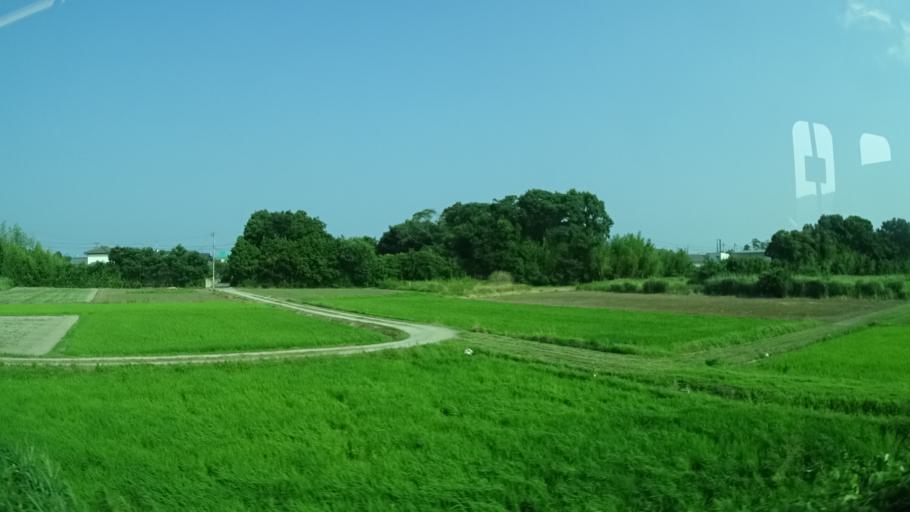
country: JP
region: Fukushima
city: Iwaki
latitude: 37.0813
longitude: 140.9583
